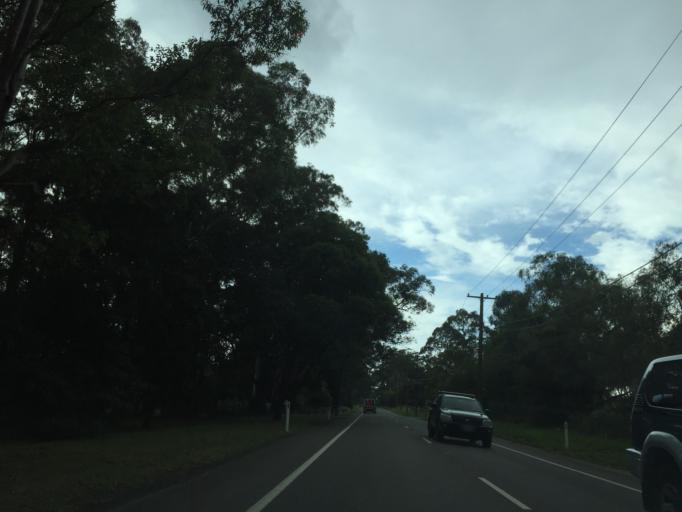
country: AU
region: New South Wales
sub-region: Hornsby Shire
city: Galston
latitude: -33.6734
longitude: 151.0345
